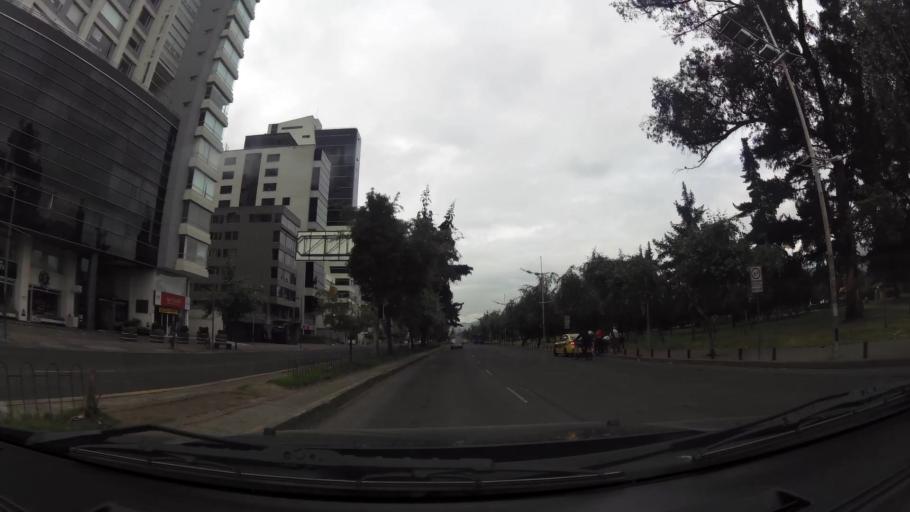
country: EC
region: Pichincha
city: Quito
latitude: -0.1773
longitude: -78.4810
